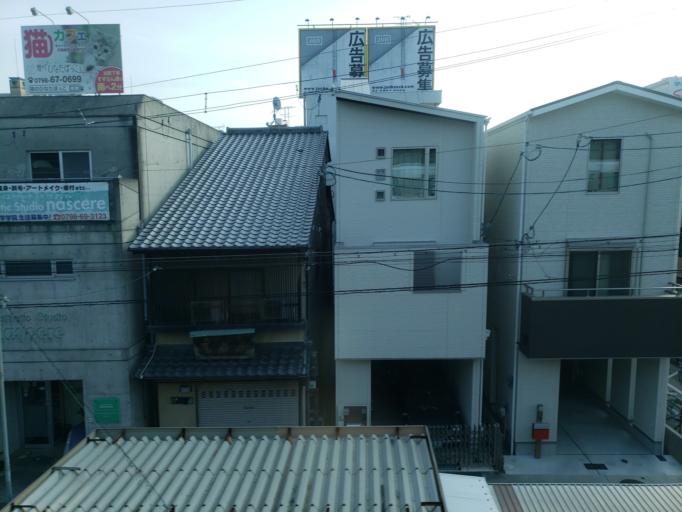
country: JP
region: Hyogo
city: Amagasaki
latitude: 34.7388
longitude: 135.3744
